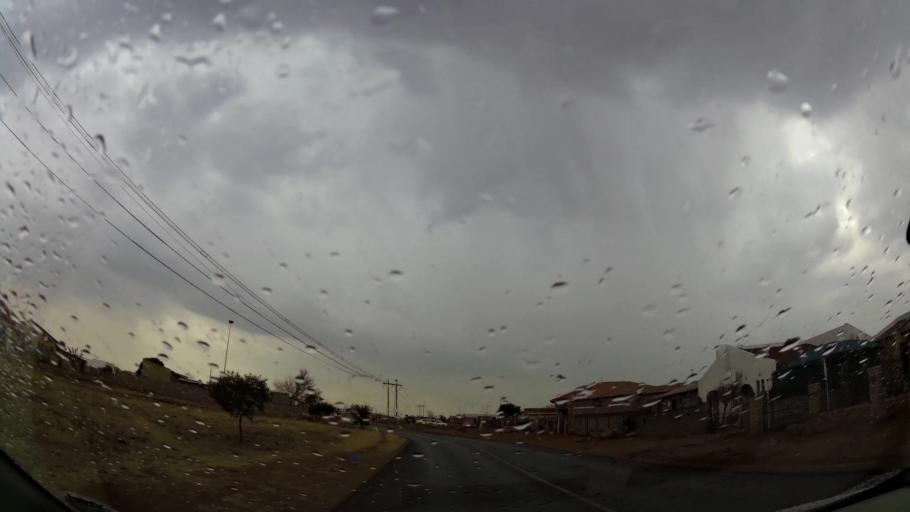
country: ZA
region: Gauteng
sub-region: Ekurhuleni Metropolitan Municipality
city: Germiston
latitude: -26.3589
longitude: 28.1577
